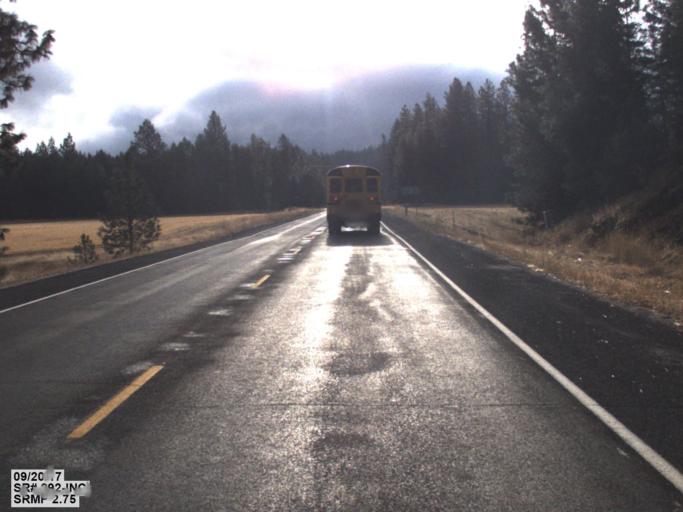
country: US
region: Washington
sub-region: Stevens County
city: Chewelah
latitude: 48.0648
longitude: -117.6857
